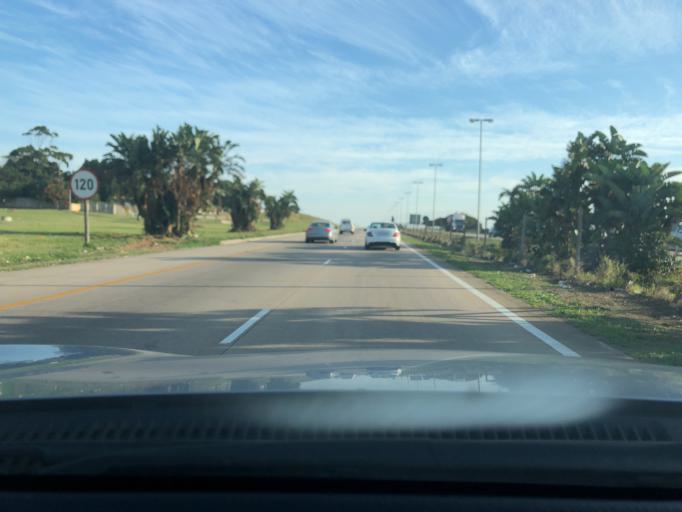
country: ZA
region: KwaZulu-Natal
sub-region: iLembe District Municipality
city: Stanger
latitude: -29.4056
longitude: 31.2841
